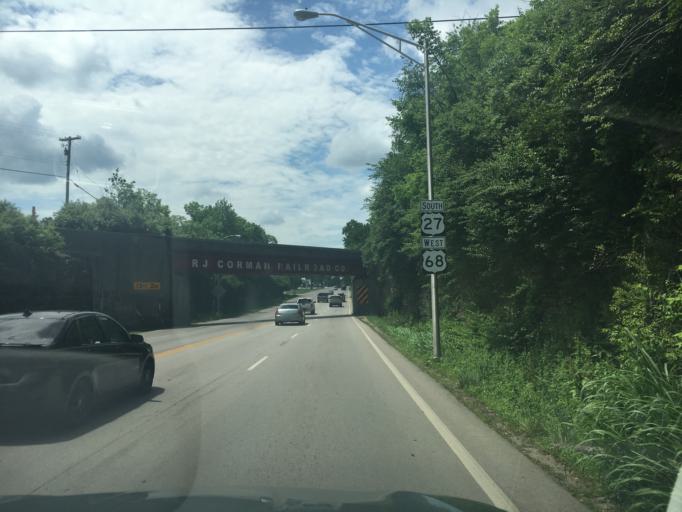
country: US
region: Kentucky
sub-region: Fayette County
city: Lexington-Fayette
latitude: 38.0672
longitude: -84.4736
